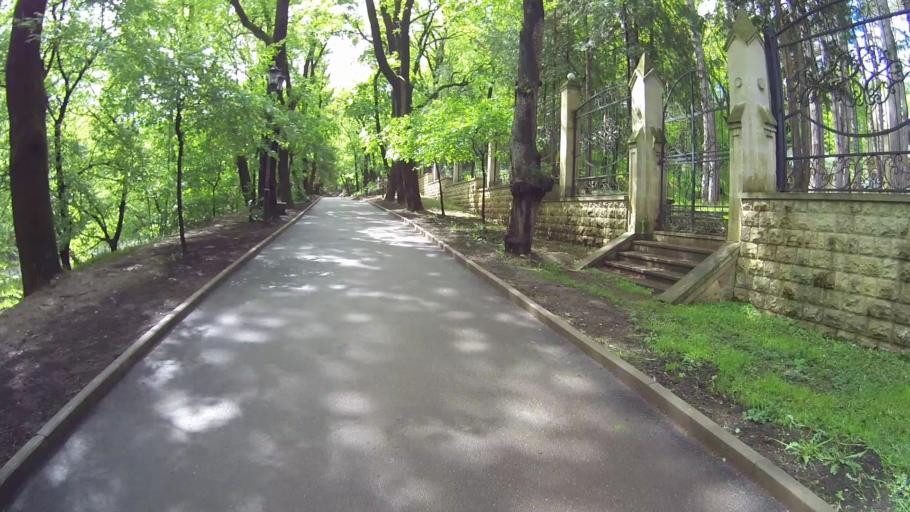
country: RU
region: Stavropol'skiy
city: Kislovodsk
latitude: 43.8964
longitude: 42.7176
